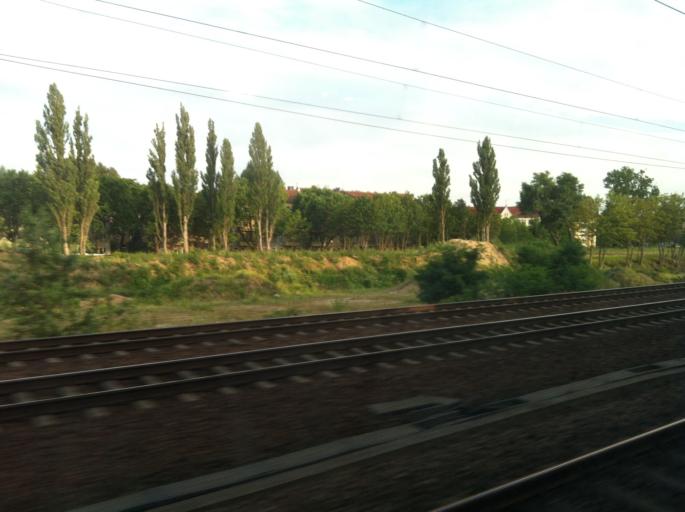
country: DE
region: Berlin
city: Pankow
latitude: 52.5683
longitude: 13.4140
